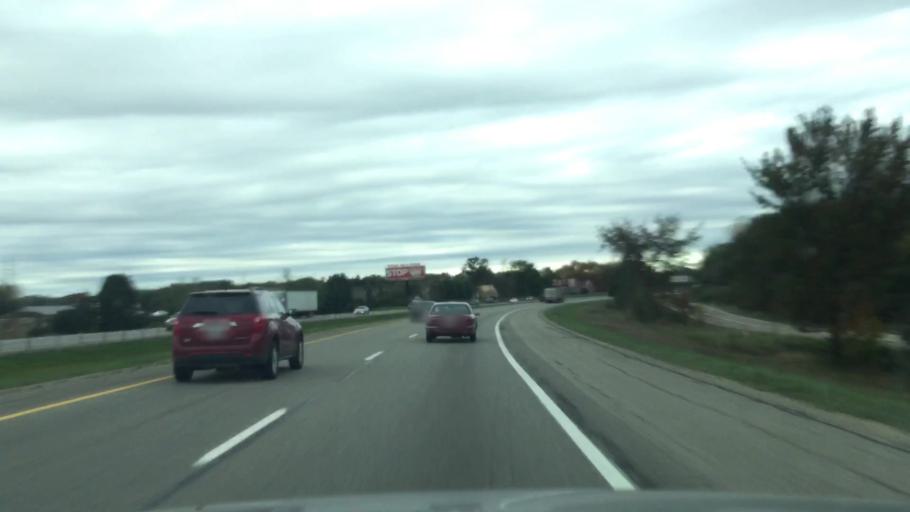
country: US
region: Michigan
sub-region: Livingston County
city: Brighton
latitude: 42.6172
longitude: -83.7461
